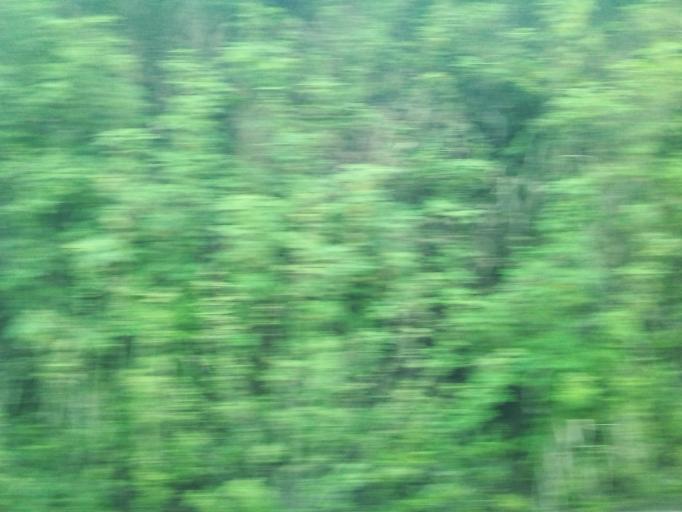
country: BR
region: Minas Gerais
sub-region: Joao Monlevade
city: Joao Monlevade
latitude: -19.8526
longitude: -43.1208
